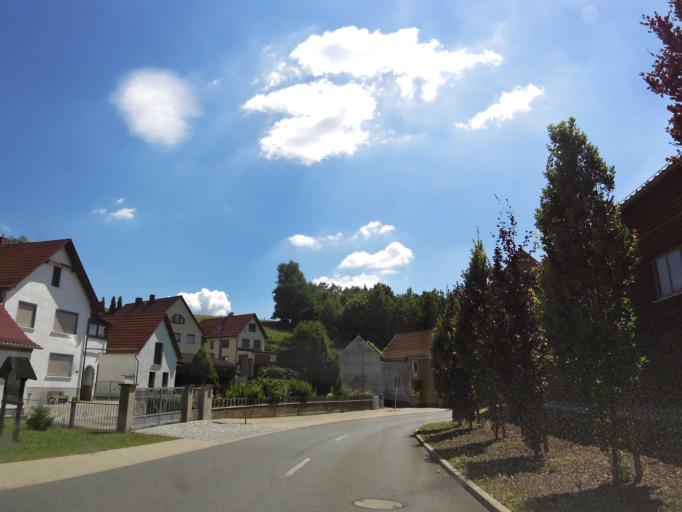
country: DE
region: Thuringia
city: Reichenbach
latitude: 50.8876
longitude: 11.8988
